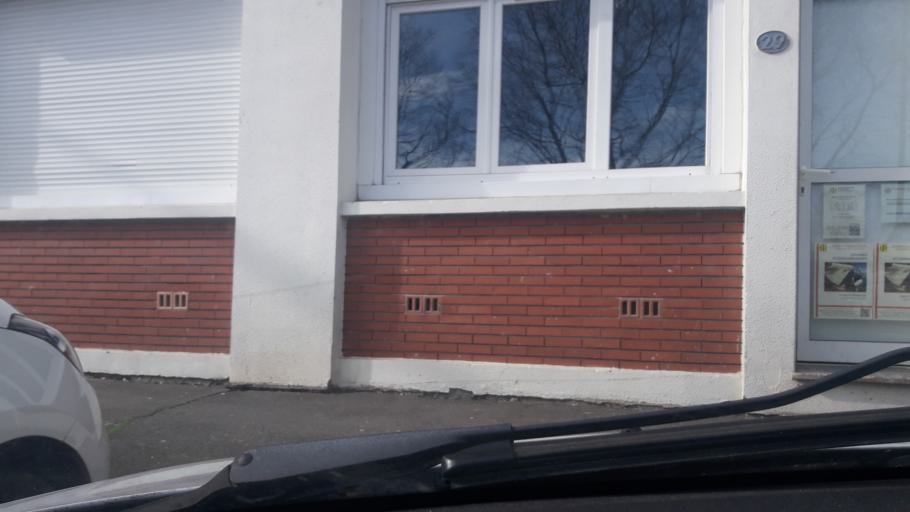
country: FR
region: Midi-Pyrenees
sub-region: Departement de la Haute-Garonne
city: Toulouse
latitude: 43.5813
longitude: 1.4276
